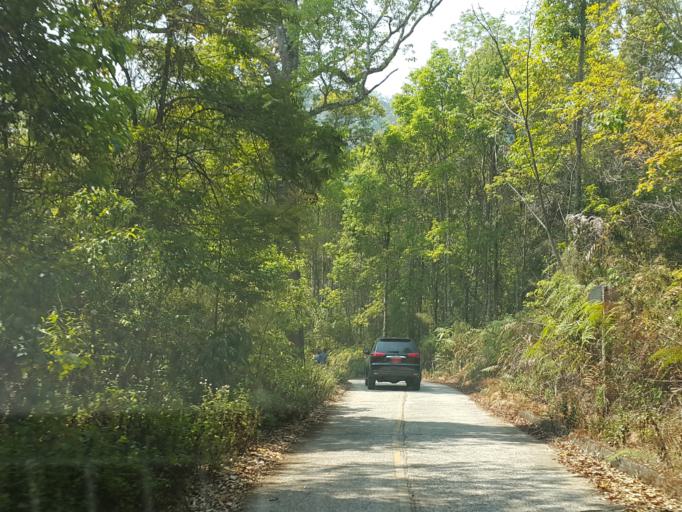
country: TH
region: Chiang Mai
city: Mae On
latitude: 18.8457
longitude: 99.3752
